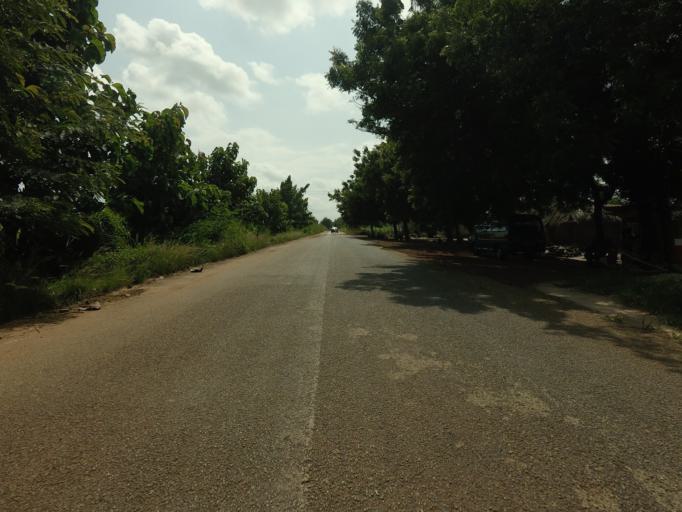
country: TG
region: Maritime
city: Lome
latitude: 6.2639
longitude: 0.9547
